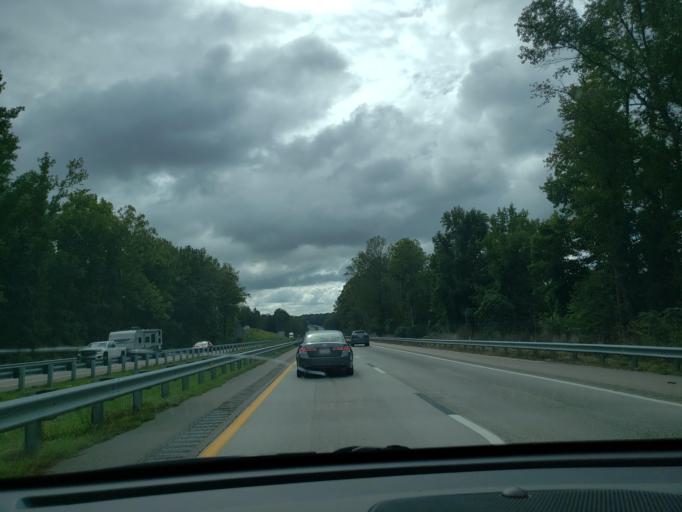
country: US
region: North Carolina
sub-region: Warren County
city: Norlina
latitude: 36.4204
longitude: -78.3104
